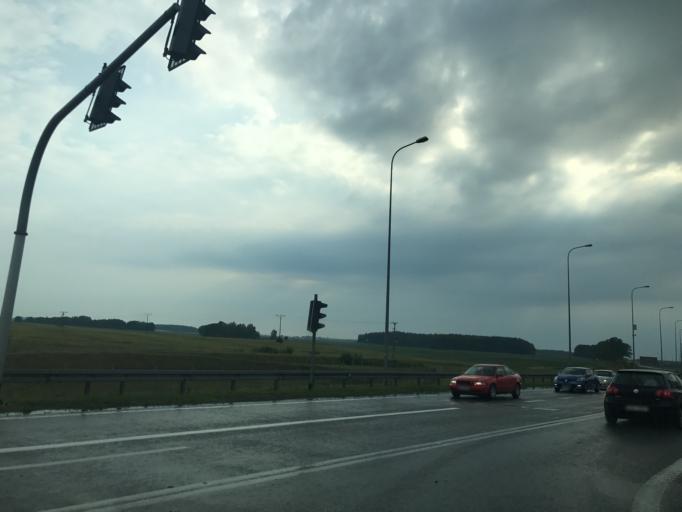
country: PL
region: Pomeranian Voivodeship
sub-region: Powiat chojnicki
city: Chojnice
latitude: 53.6888
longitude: 17.4739
